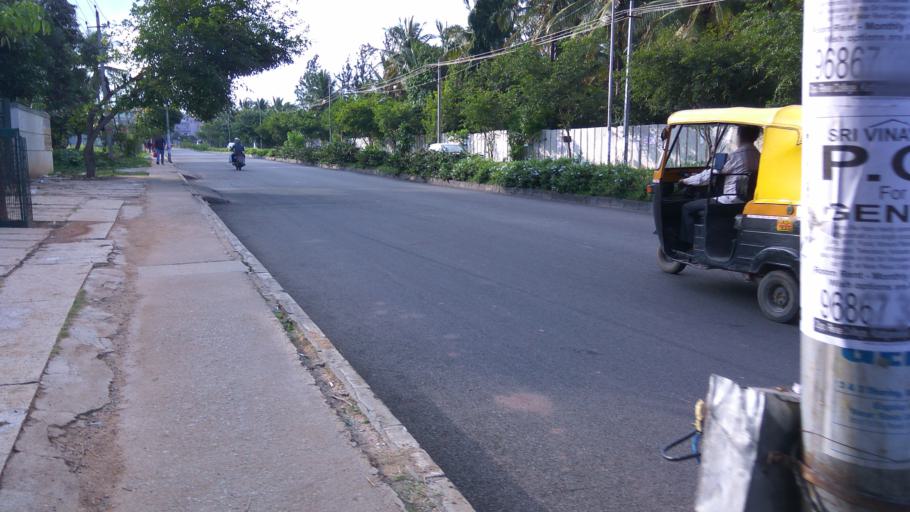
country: IN
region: Karnataka
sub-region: Bangalore Urban
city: Yelahanka
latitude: 13.1201
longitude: 77.6322
